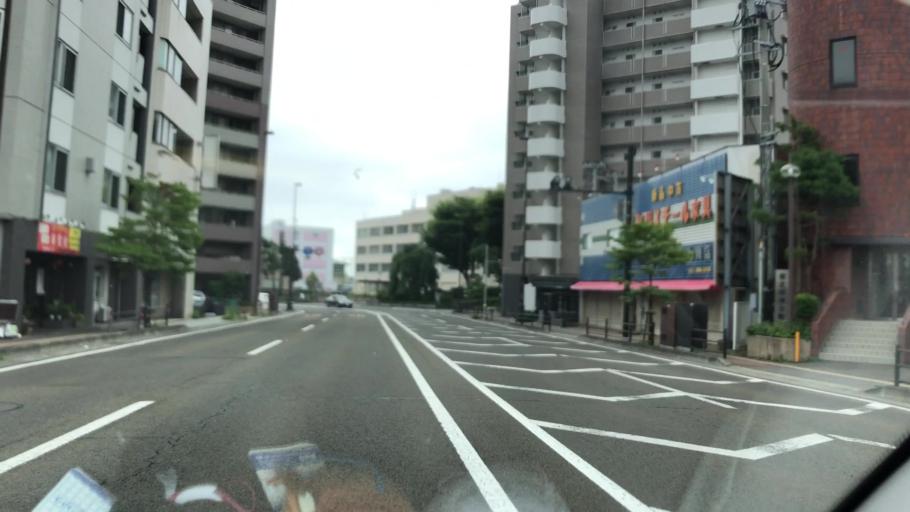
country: JP
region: Miyagi
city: Sendai-shi
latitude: 38.2633
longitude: 140.8970
